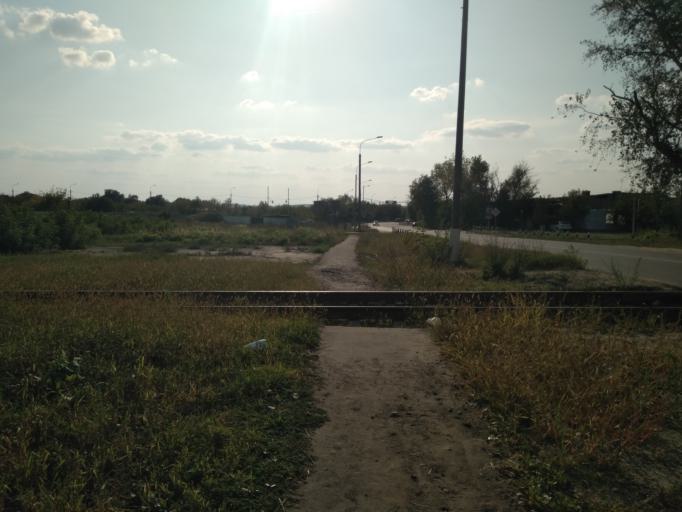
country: RU
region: Moskovskaya
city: Zhukovskiy
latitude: 55.5732
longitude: 38.1174
